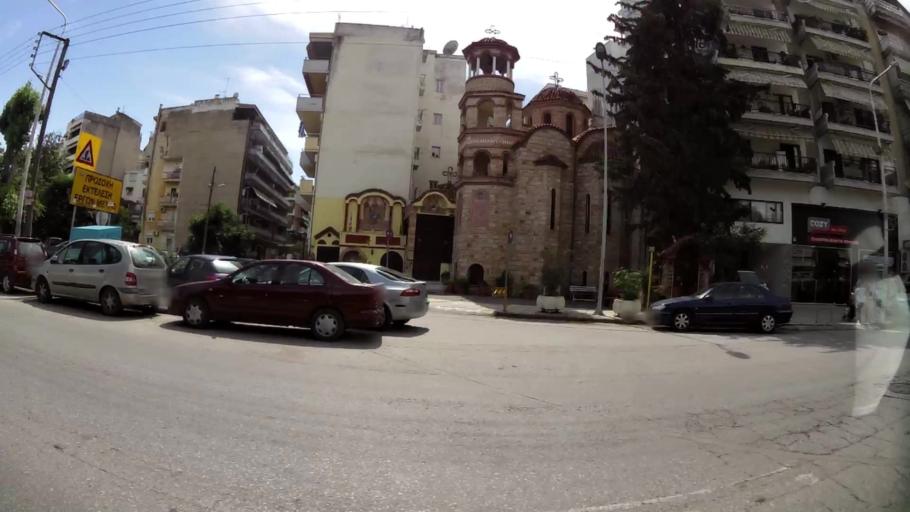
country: GR
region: Central Macedonia
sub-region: Nomos Thessalonikis
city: Triandria
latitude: 40.6025
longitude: 22.9589
